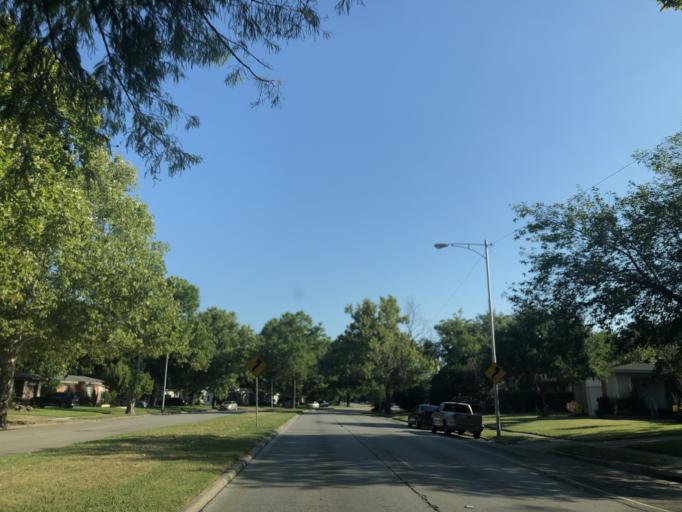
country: US
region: Texas
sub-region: Dallas County
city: Grand Prairie
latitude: 32.7498
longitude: -97.0173
